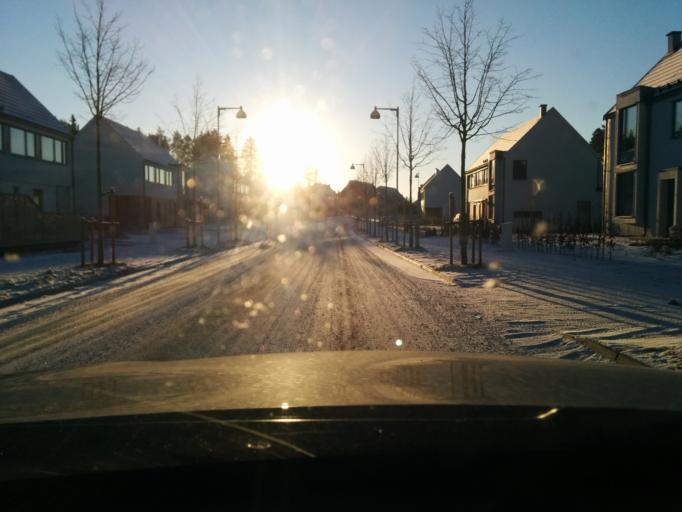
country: SE
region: Stockholm
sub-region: Vallentuna Kommun
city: Vallentuna
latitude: 59.5029
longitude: 18.0882
